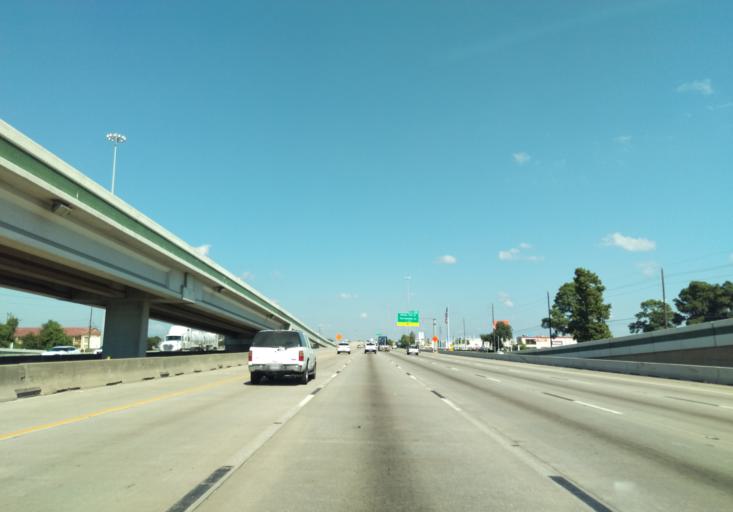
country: US
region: Texas
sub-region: Harris County
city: Spring
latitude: 30.0136
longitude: -95.4280
